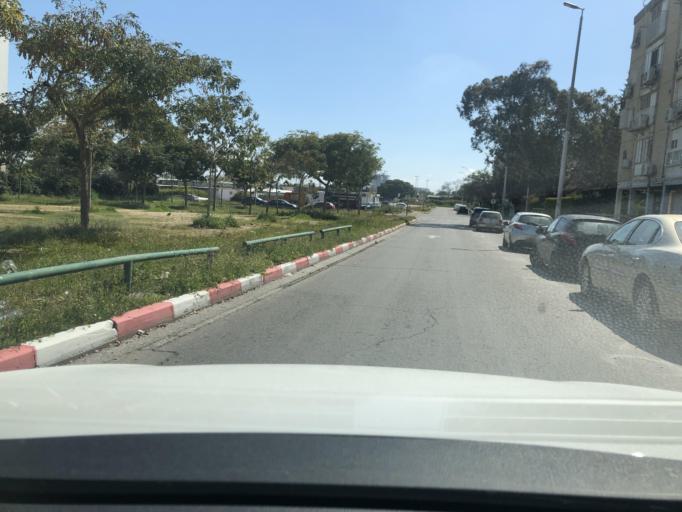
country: IL
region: Tel Aviv
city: Bat Yam
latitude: 32.0076
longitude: 34.7570
